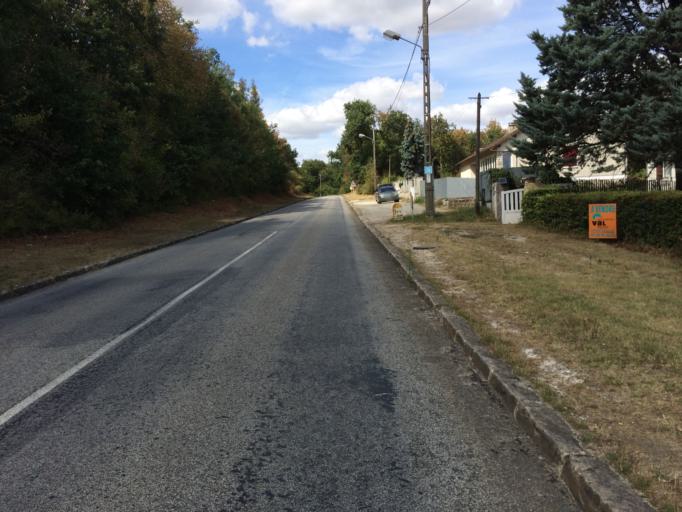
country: FR
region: Ile-de-France
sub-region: Departement de l'Essonne
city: Maisse
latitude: 48.3860
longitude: 2.3764
